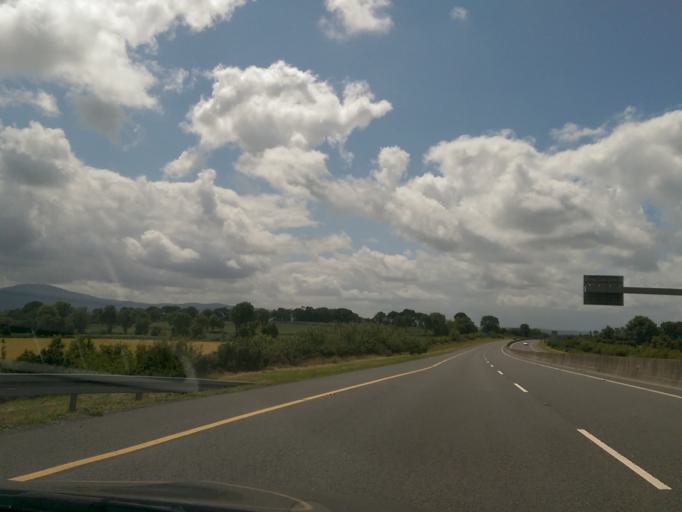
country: IE
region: Munster
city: Cahir
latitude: 52.3490
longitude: -8.0064
